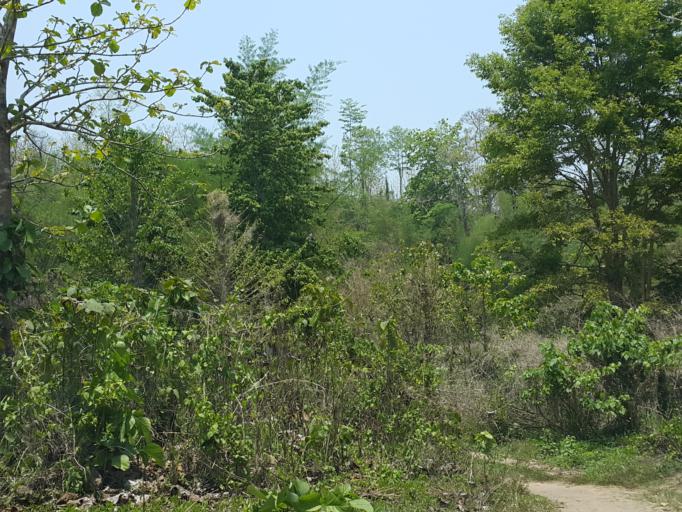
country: TH
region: Kanchanaburi
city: Sai Yok
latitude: 14.2379
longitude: 98.8716
